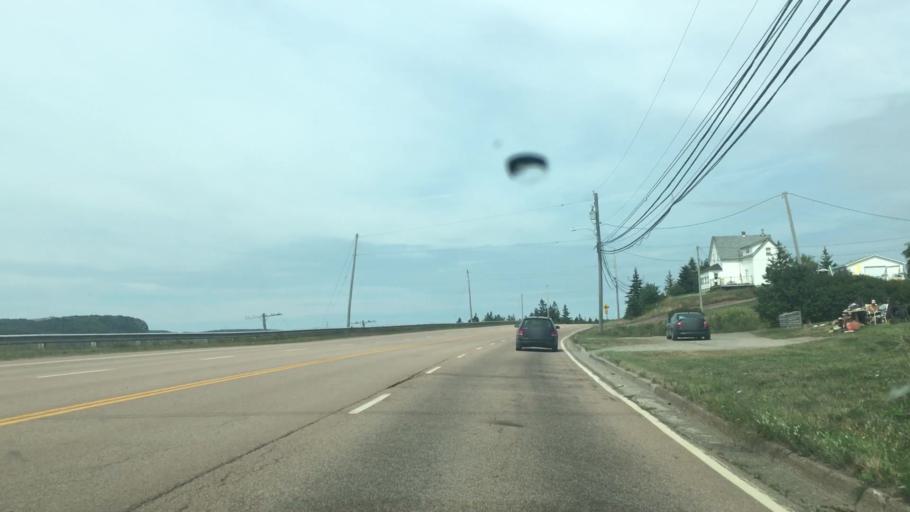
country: CA
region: Nova Scotia
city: Port Hawkesbury
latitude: 45.6267
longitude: -61.3721
